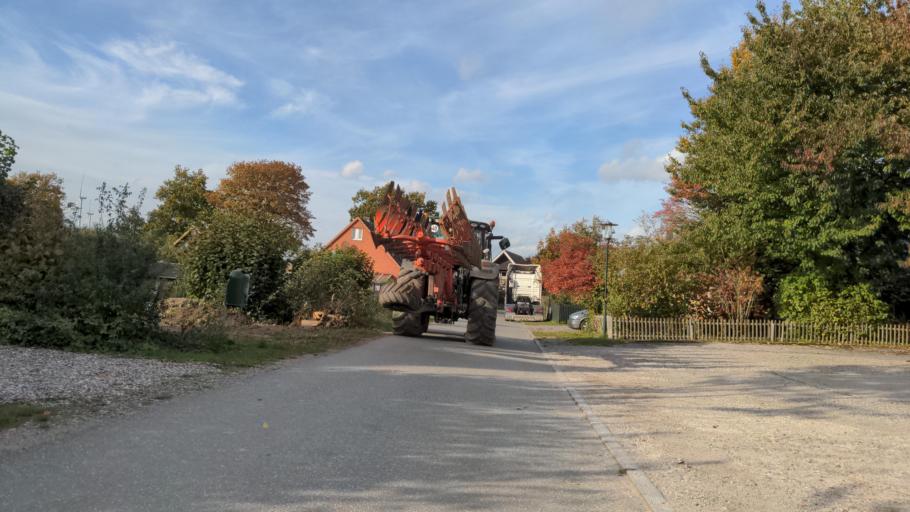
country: DE
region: Schleswig-Holstein
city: Monkhagen
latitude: 53.9476
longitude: 10.5636
